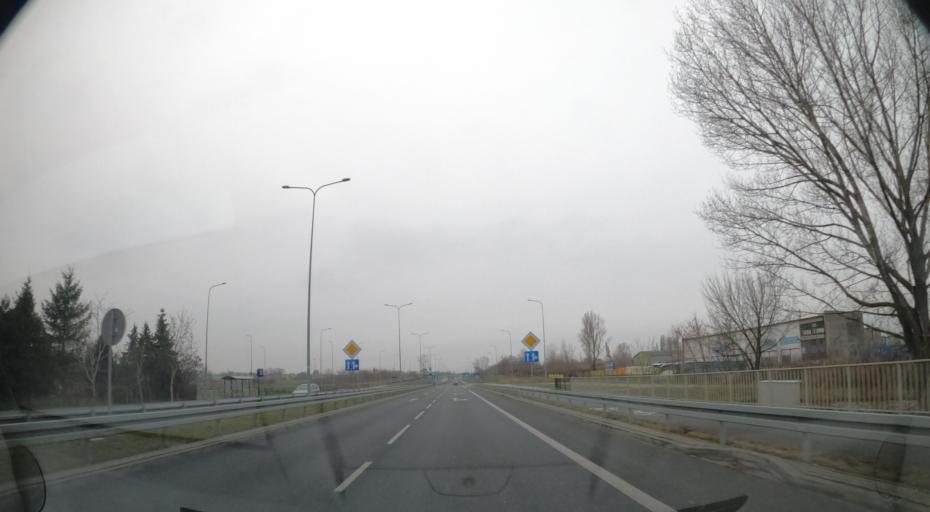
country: PL
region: Masovian Voivodeship
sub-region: Radom
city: Radom
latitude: 51.4037
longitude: 21.2008
